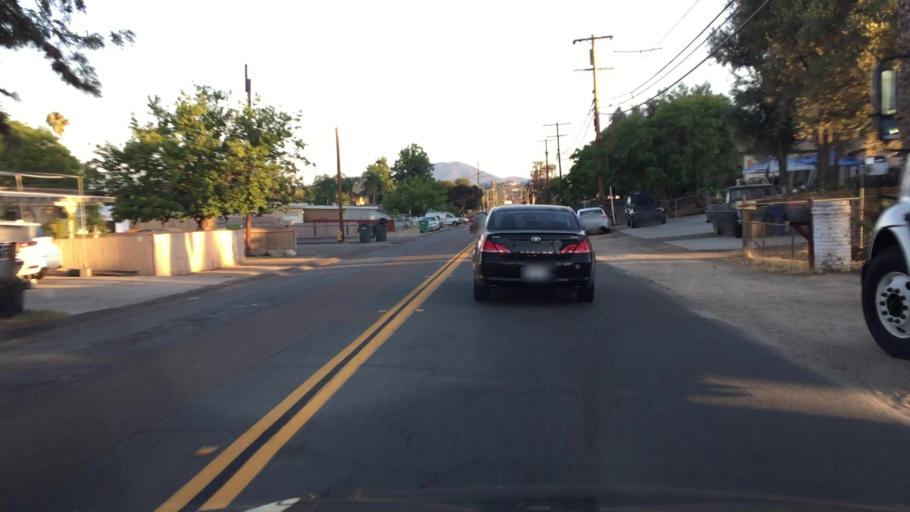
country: US
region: California
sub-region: San Diego County
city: Bostonia
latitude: 32.8109
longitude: -116.9446
